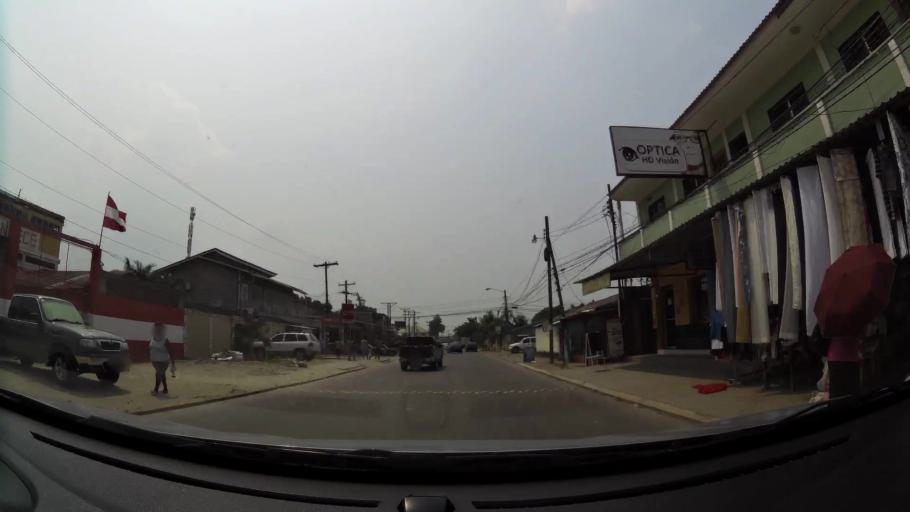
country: HN
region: Cortes
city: La Lima
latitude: 15.4396
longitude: -87.9261
